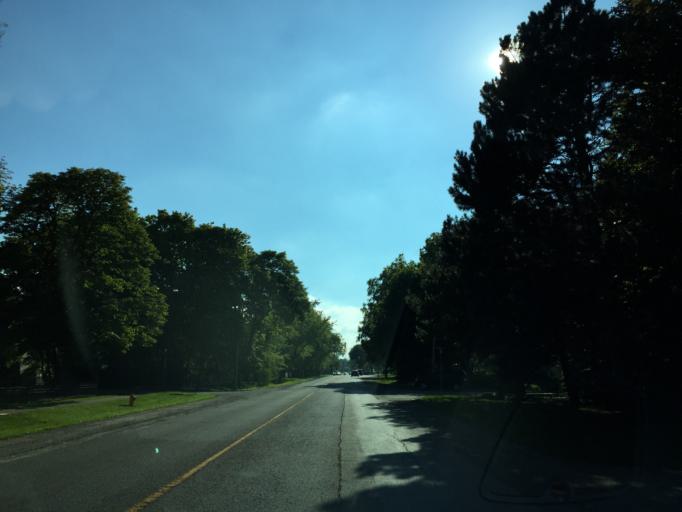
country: US
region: New York
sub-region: Niagara County
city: Youngstown
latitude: 43.2546
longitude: -79.0823
